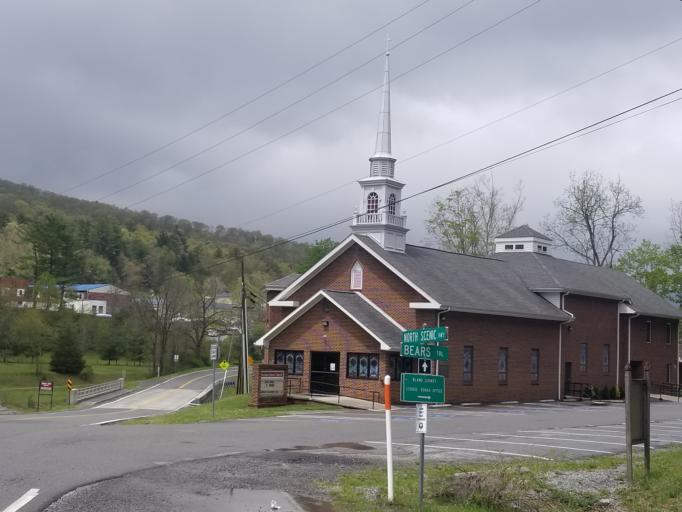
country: US
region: Virginia
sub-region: Bland County
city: Bland
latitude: 37.1521
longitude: -81.1499
